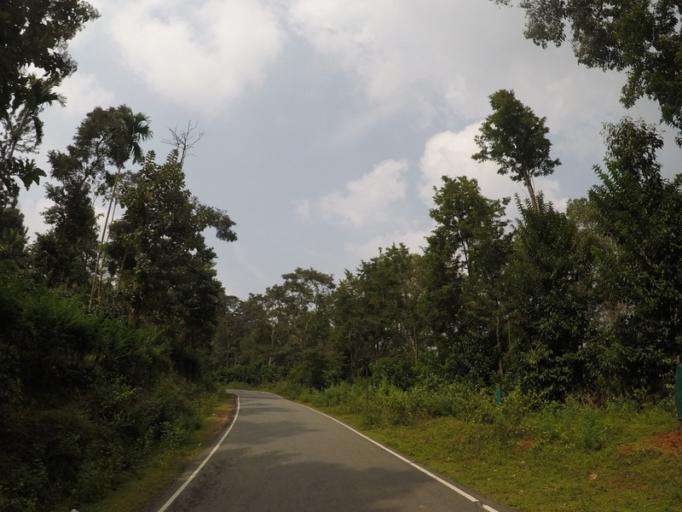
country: IN
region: Karnataka
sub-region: Chikmagalur
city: Sringeri
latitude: 13.2364
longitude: 75.3768
